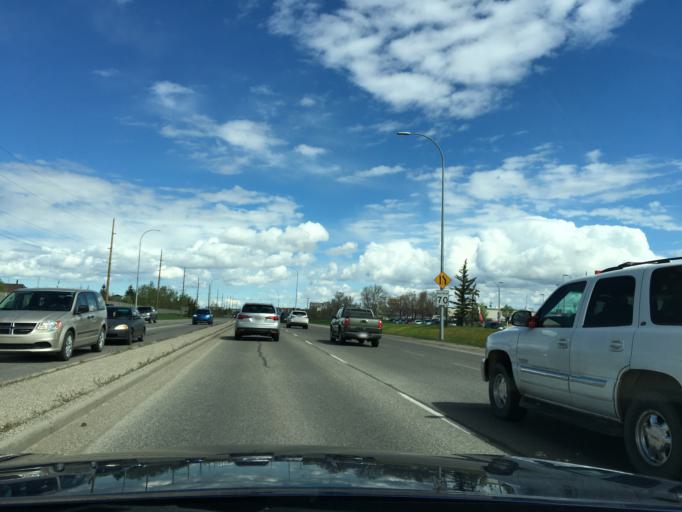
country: CA
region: Alberta
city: Calgary
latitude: 51.0589
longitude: -114.0017
